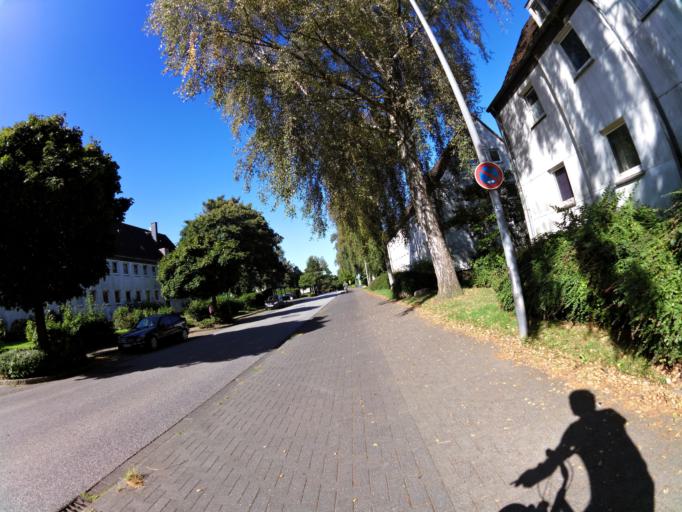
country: DE
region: Schleswig-Holstein
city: Barkelsby
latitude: 54.4850
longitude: 9.8282
